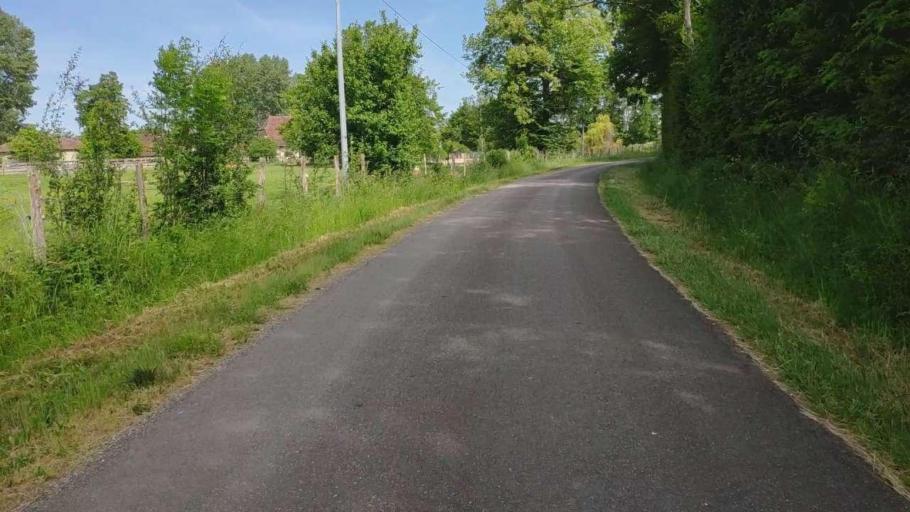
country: FR
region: Franche-Comte
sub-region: Departement du Jura
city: Bletterans
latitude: 46.6791
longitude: 5.4085
